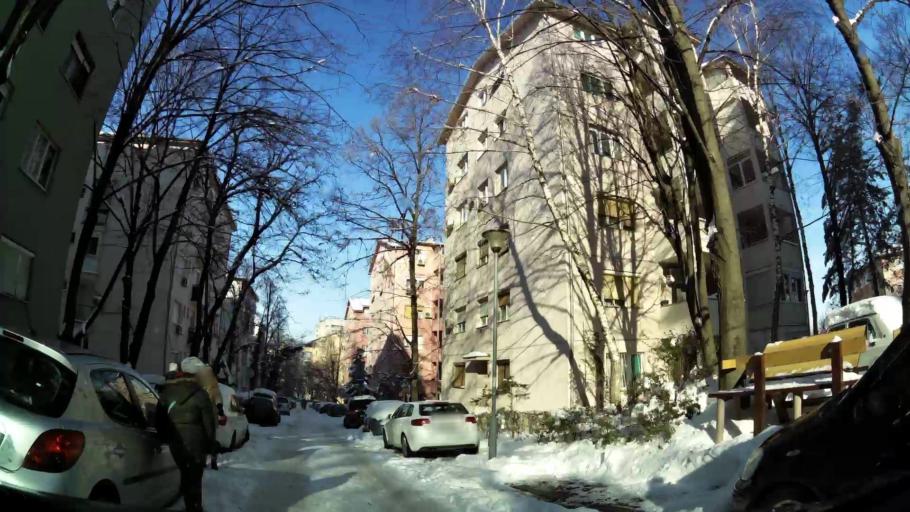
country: RS
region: Central Serbia
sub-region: Belgrade
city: Palilula
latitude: 44.8137
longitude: 20.5194
